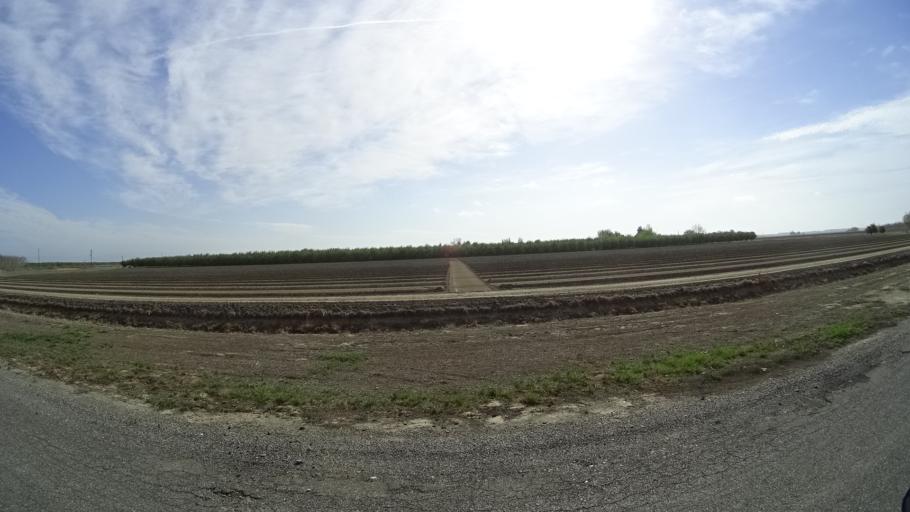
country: US
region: California
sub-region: Glenn County
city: Hamilton City
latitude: 39.6289
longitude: -122.0462
